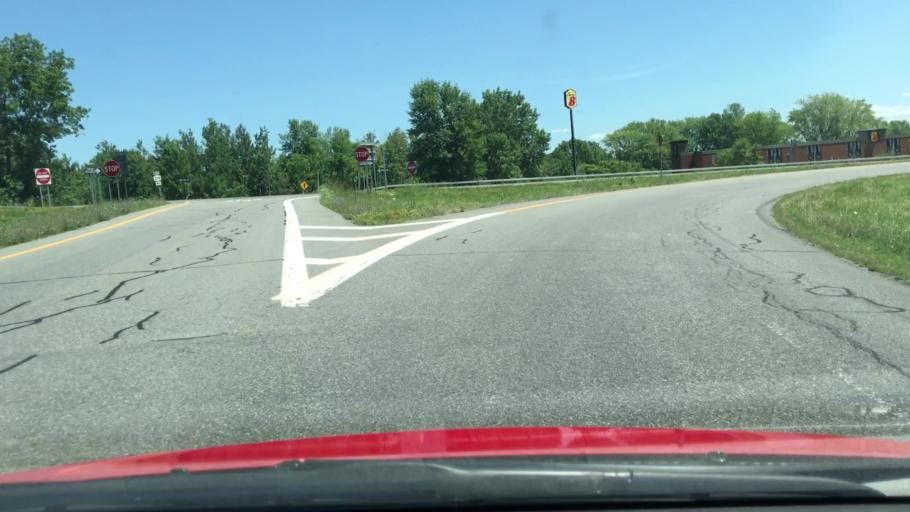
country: US
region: New York
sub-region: Clinton County
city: Plattsburgh
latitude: 44.7272
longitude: -73.4396
